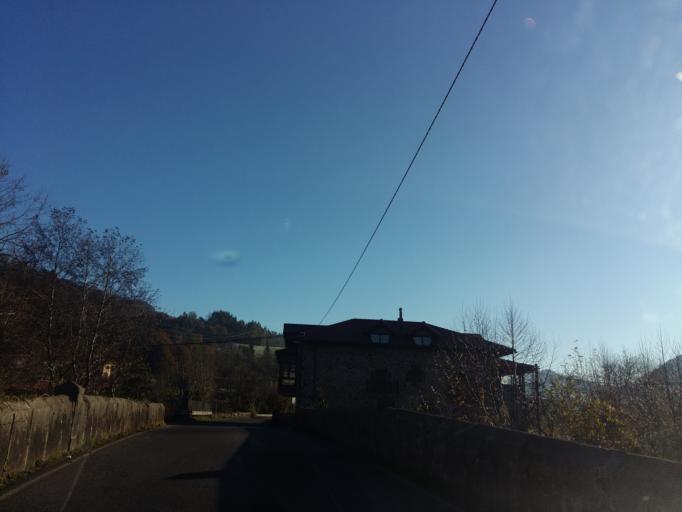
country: ES
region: Cantabria
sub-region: Provincia de Cantabria
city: Ramales de la Victoria
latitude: 43.2778
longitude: -3.5256
